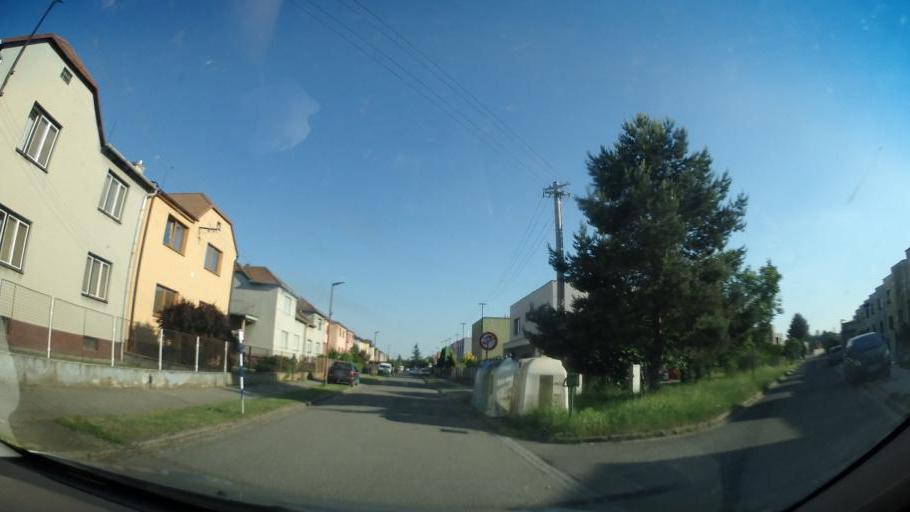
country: CZ
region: Zlin
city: Chropyne
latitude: 49.3671
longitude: 17.3601
